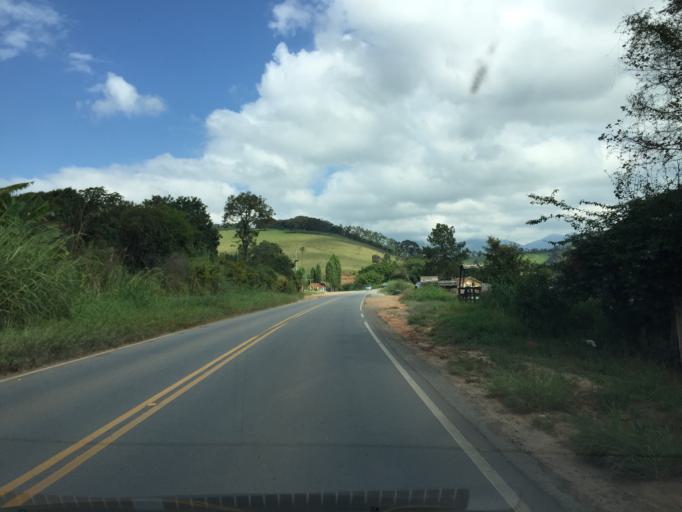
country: BR
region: Minas Gerais
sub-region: Passa Quatro
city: Passa Quatro
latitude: -22.3650
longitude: -44.9547
